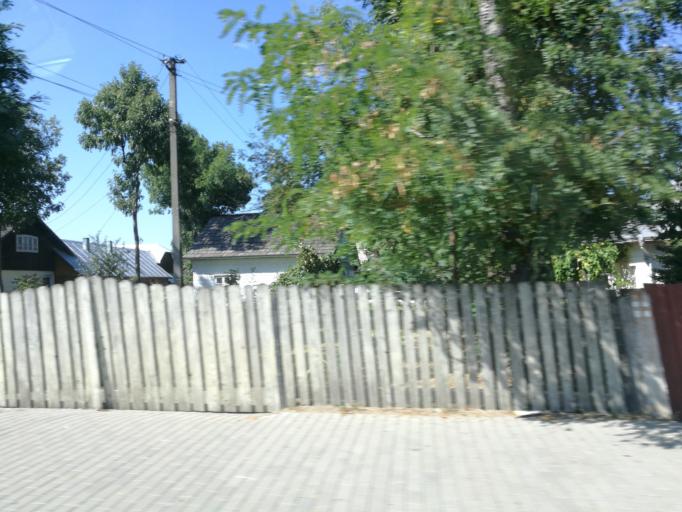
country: RO
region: Suceava
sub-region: Comuna Marginea
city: Marginea
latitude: 47.8077
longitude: 25.8182
